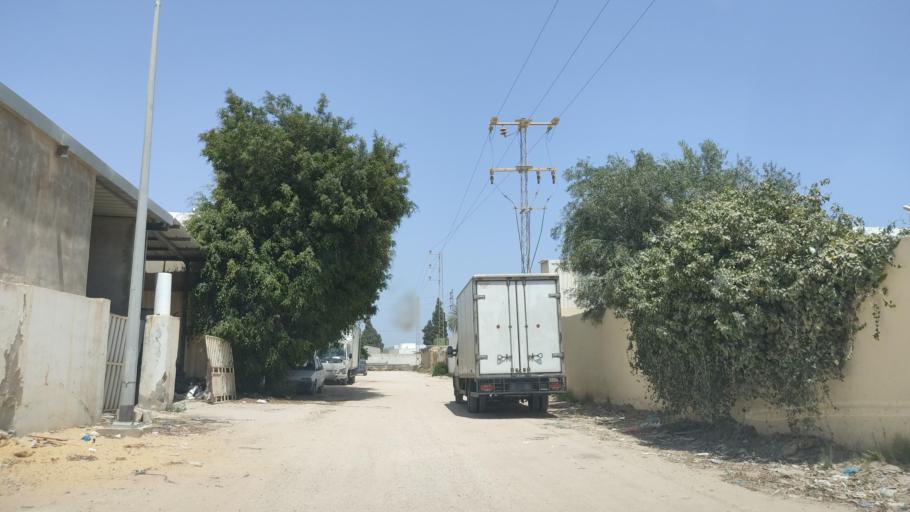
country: TN
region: Safaqis
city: Sfax
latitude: 34.7097
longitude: 10.7278
